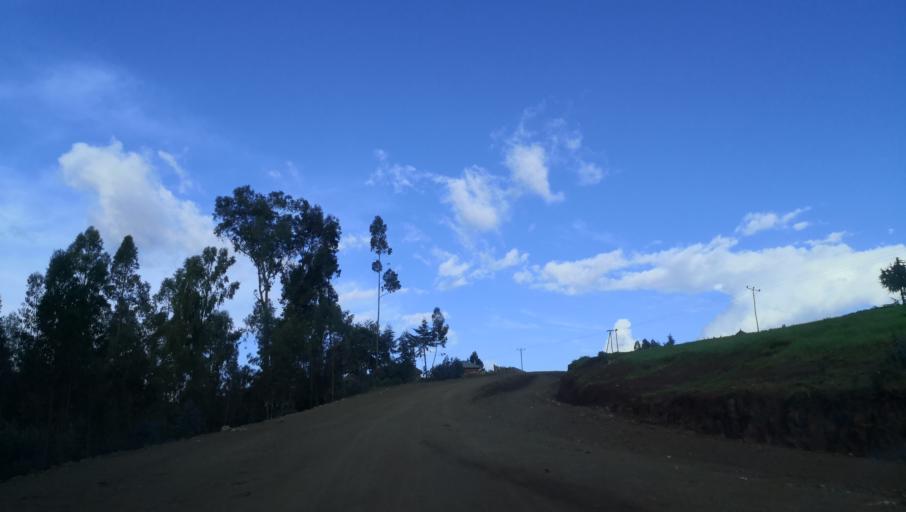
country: ET
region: Southern Nations, Nationalities, and People's Region
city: Butajira
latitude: 8.3920
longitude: 38.2964
